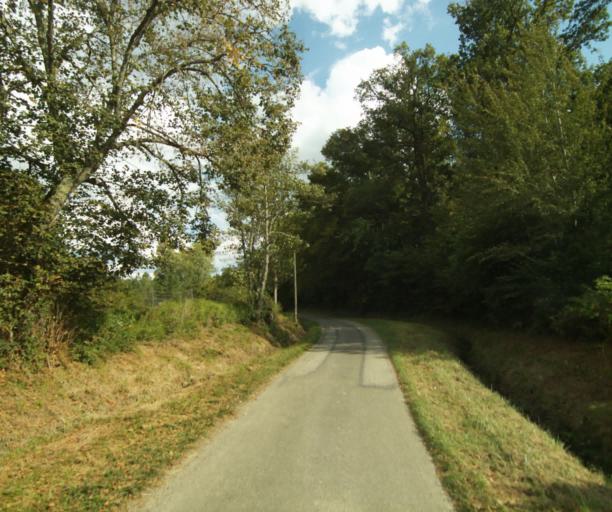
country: FR
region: Midi-Pyrenees
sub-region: Departement du Gers
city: Cazaubon
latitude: 43.9228
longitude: -0.0511
